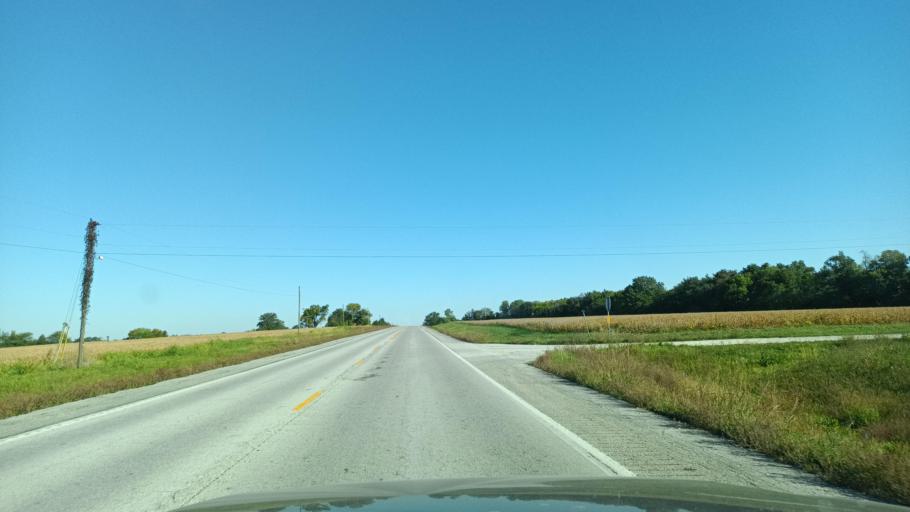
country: US
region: Missouri
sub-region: Audrain County
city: Vandalia
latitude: 39.3382
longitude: -91.6430
